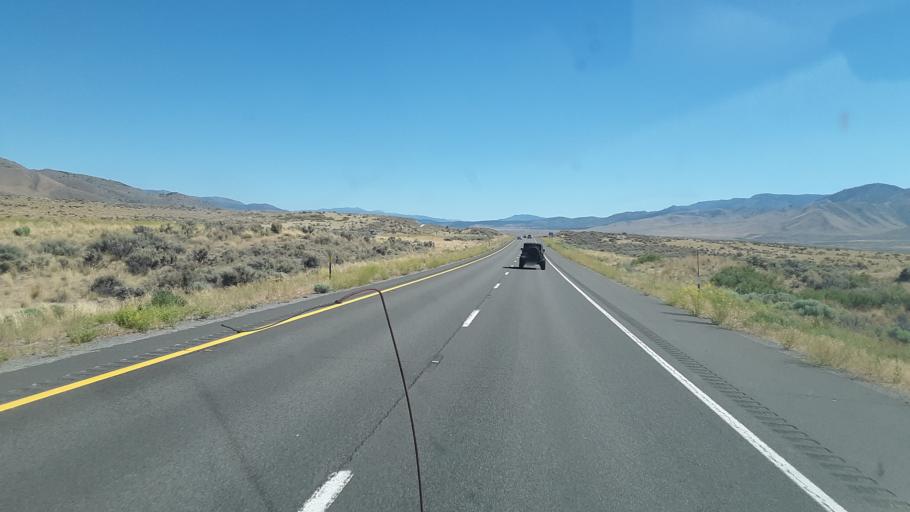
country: US
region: Nevada
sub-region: Washoe County
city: Cold Springs
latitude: 39.7552
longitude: -120.0394
